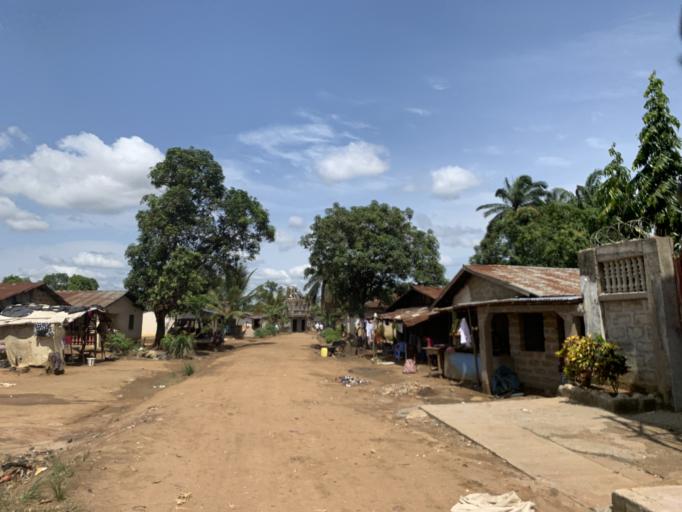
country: SL
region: Western Area
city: Waterloo
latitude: 8.3392
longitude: -13.0483
